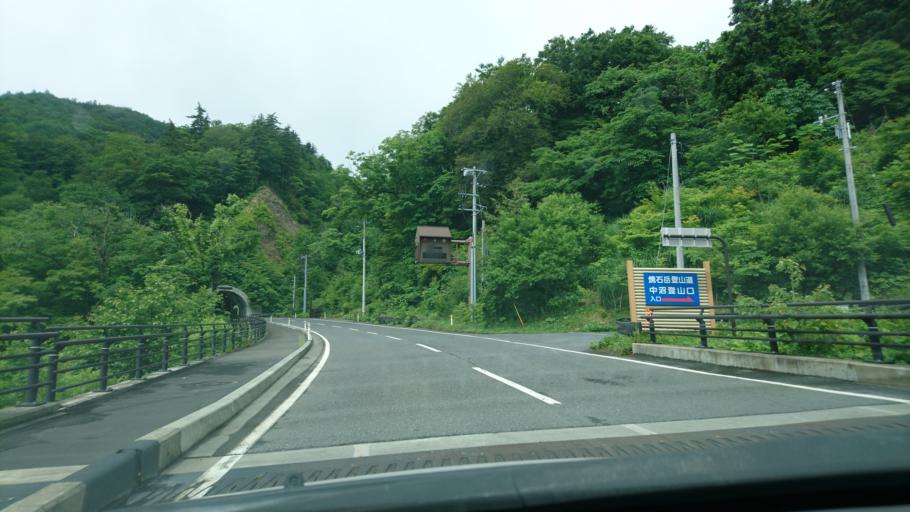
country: JP
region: Iwate
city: Mizusawa
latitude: 39.1252
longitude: 140.9096
